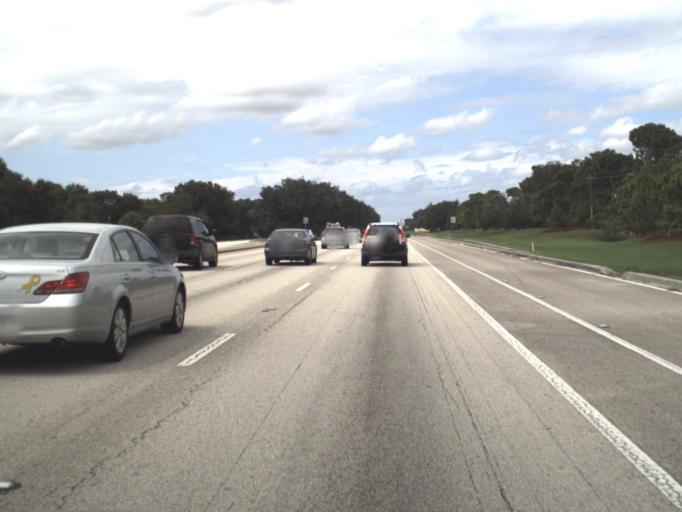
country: US
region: Florida
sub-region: Sarasota County
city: Desoto Lakes
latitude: 27.3885
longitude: -82.4880
